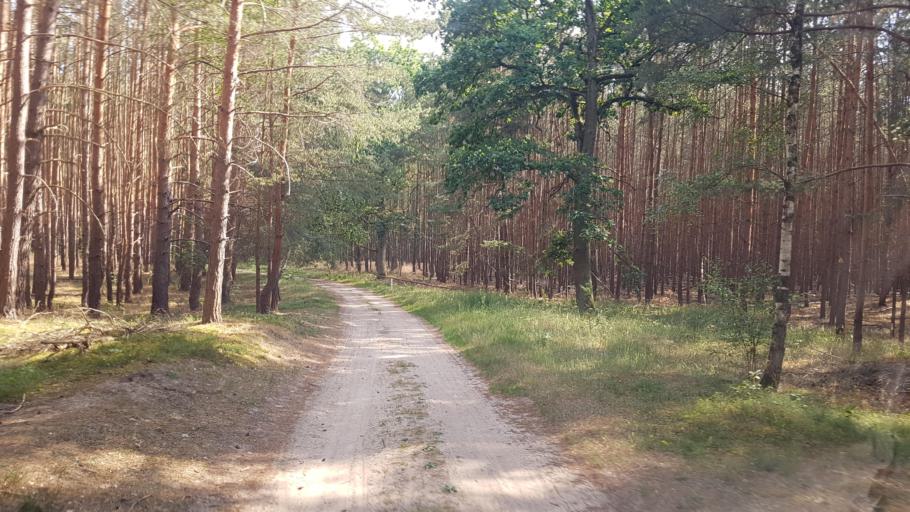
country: DE
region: Brandenburg
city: Belzig
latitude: 52.1881
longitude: 12.6052
